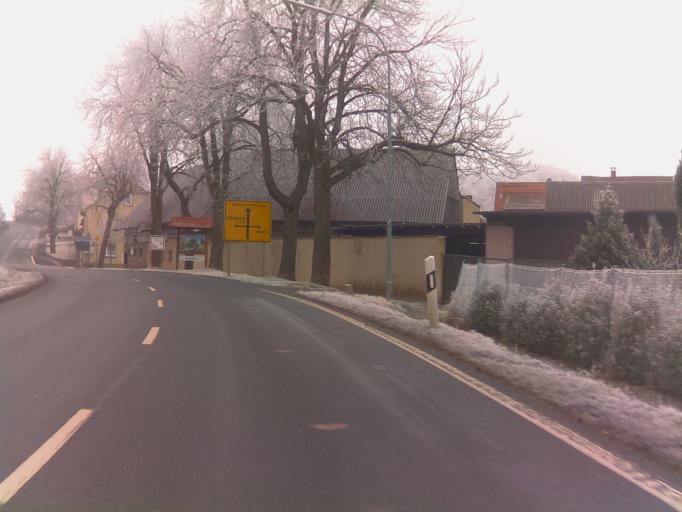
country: DE
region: Bavaria
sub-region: Regierungsbezirk Unterfranken
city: Sondheim vor der Rhoen
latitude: 50.4658
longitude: 10.1597
